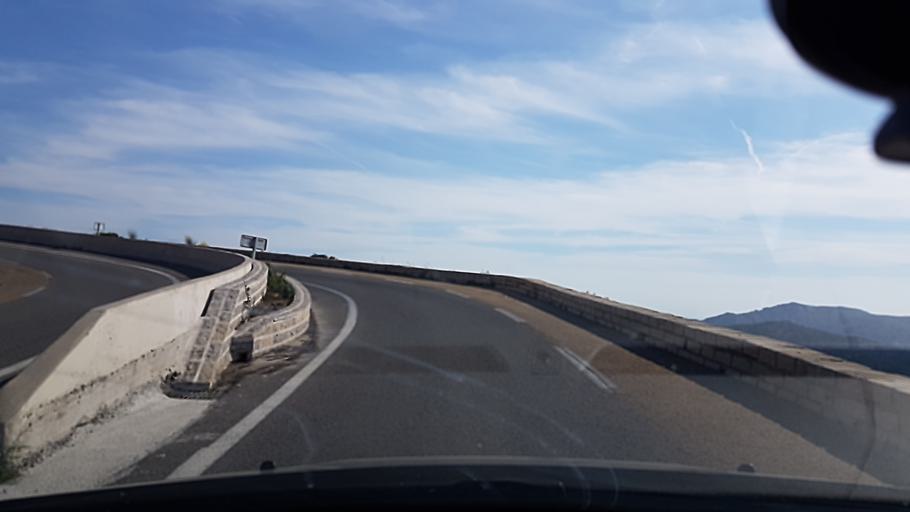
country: FR
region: Provence-Alpes-Cote d'Azur
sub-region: Departement des Bouches-du-Rhone
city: Marseille 09
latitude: 43.2403
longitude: 5.4517
